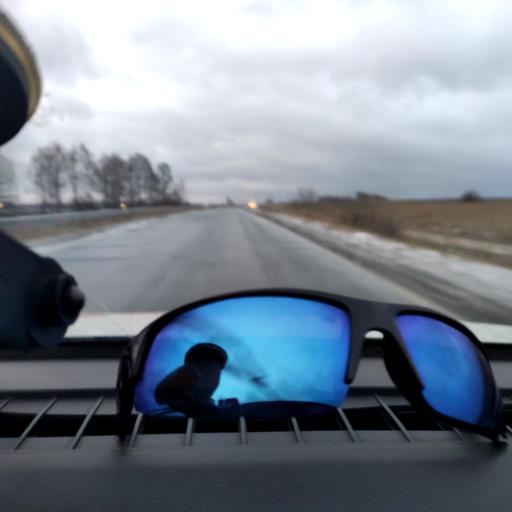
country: RU
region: Samara
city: Bereza
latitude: 53.4907
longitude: 50.1192
